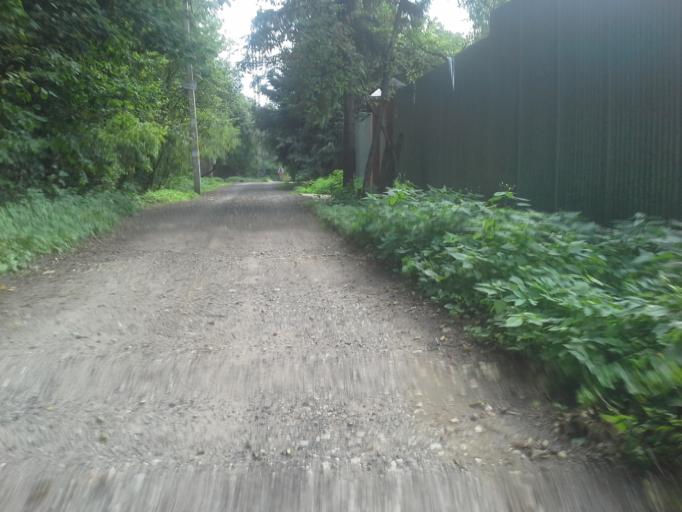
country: RU
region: Moskovskaya
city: Selyatino
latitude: 55.5336
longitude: 37.0102
